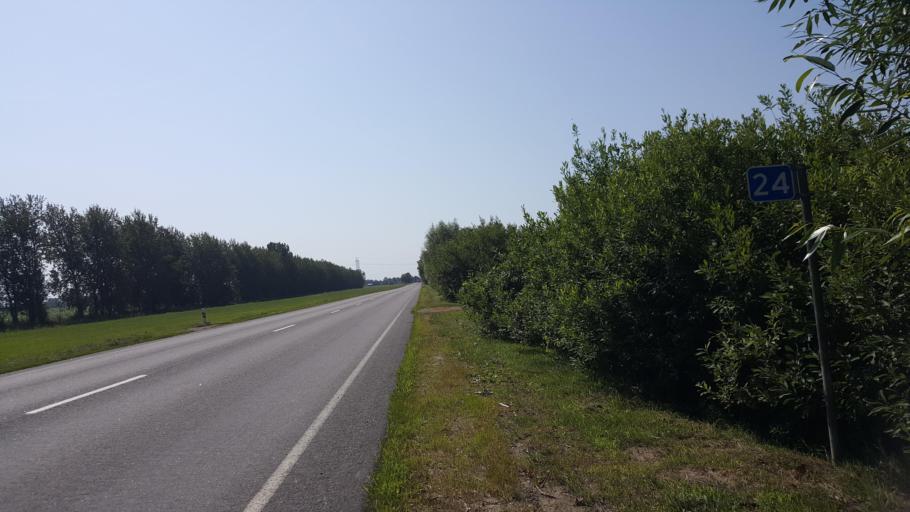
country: BY
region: Brest
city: Zhabinka
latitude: 52.2186
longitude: 23.9942
